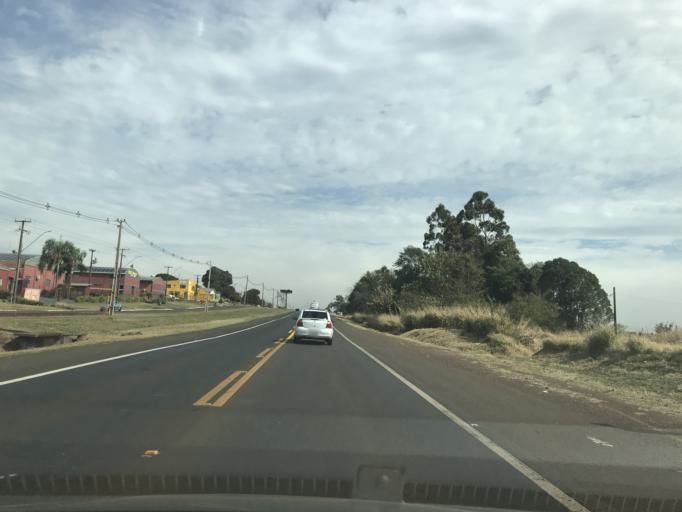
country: BR
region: Parana
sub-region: Cascavel
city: Cascavel
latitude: -25.0415
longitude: -53.6024
